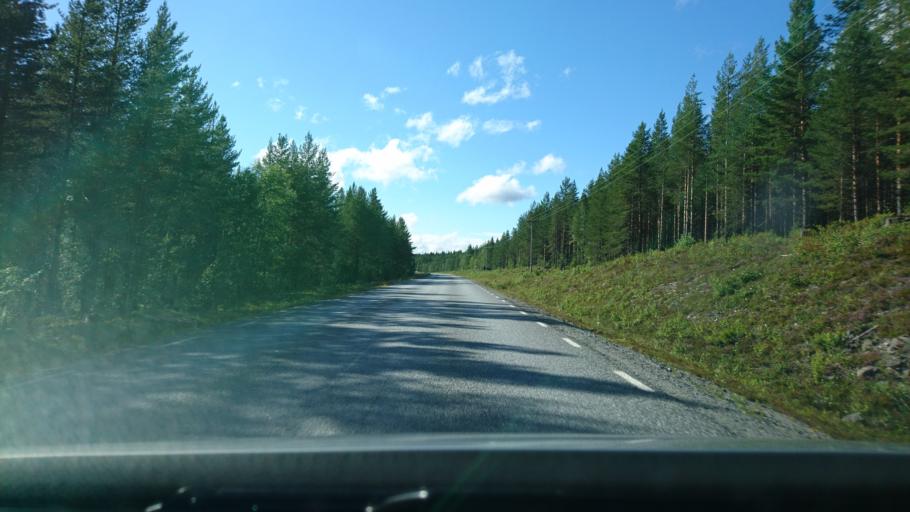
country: SE
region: Vaesterbotten
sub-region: Vilhelmina Kommun
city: Vilhelmina
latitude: 64.3639
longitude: 16.9535
